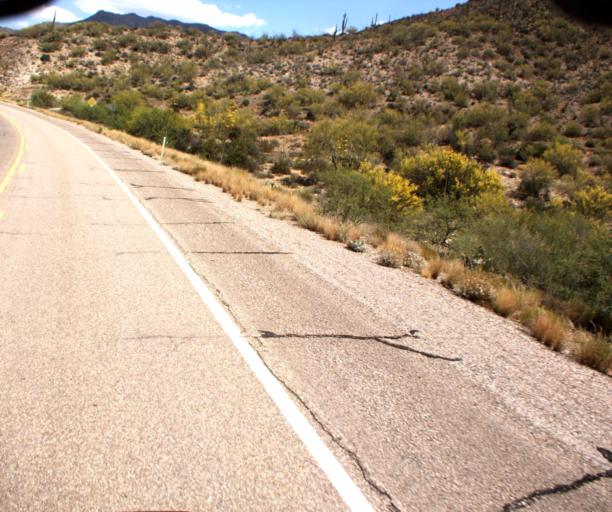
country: US
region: Arizona
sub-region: Pinal County
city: Superior
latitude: 33.2798
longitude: -111.0978
